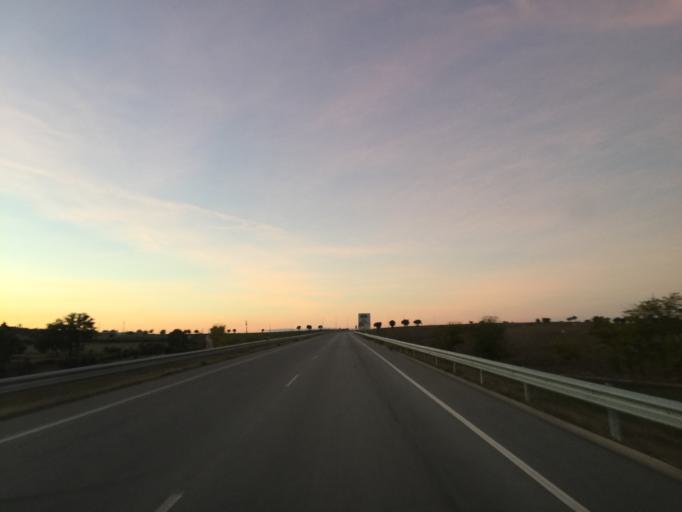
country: PT
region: Portalegre
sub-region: Alter do Chao
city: Alter do Chao
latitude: 39.3047
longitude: -7.6382
